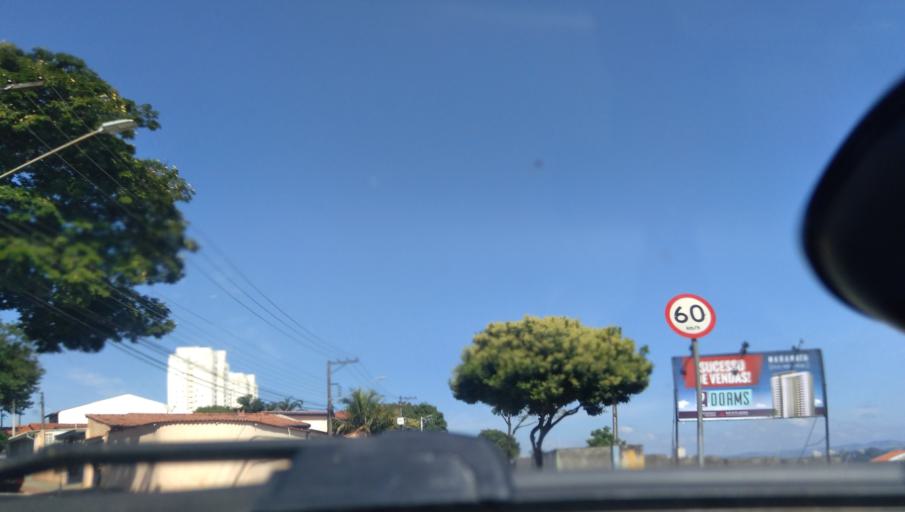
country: BR
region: Sao Paulo
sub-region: Sao Jose Dos Campos
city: Sao Jose dos Campos
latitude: -23.1779
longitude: -45.8610
